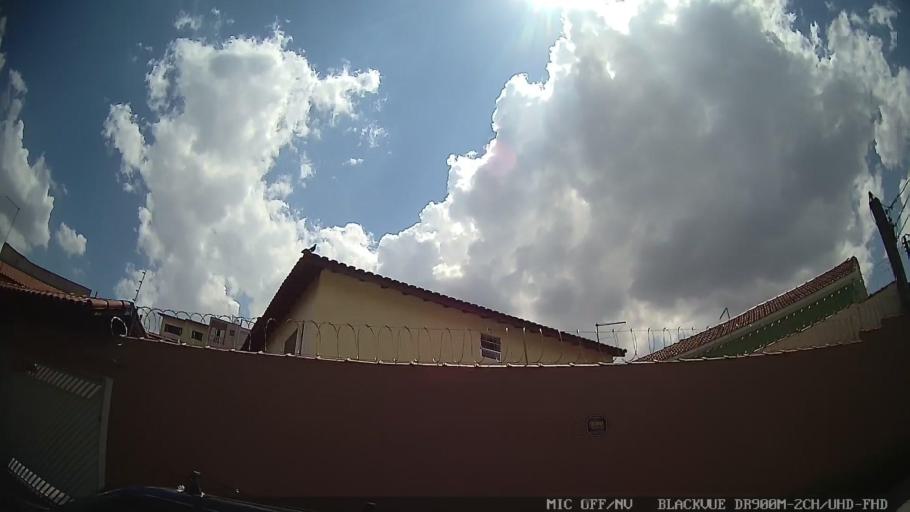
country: BR
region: Sao Paulo
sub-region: Ferraz De Vasconcelos
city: Ferraz de Vasconcelos
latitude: -23.5398
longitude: -46.4513
